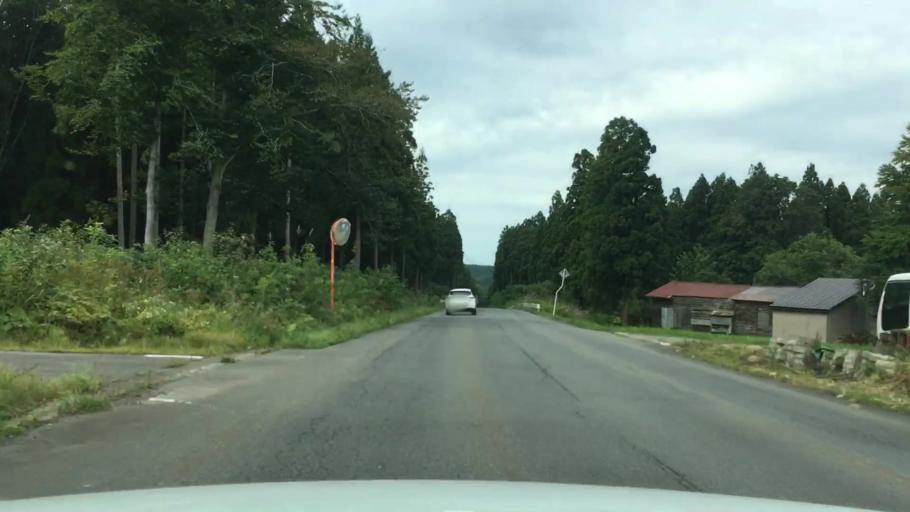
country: JP
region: Aomori
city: Shimokizukuri
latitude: 40.7104
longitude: 140.2730
